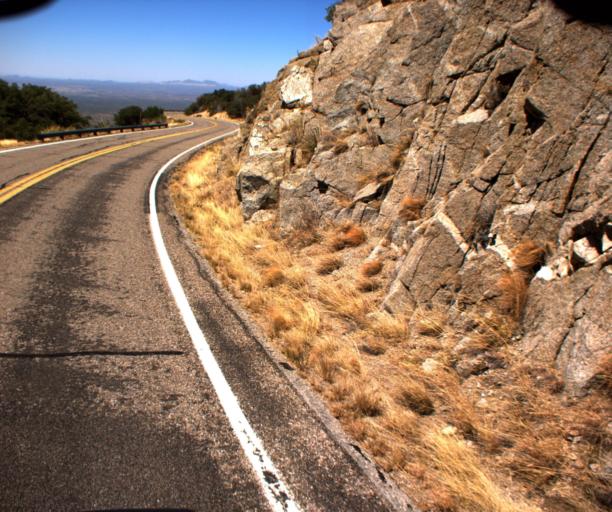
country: US
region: Arizona
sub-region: Pima County
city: Sells
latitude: 31.9700
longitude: -111.6209
